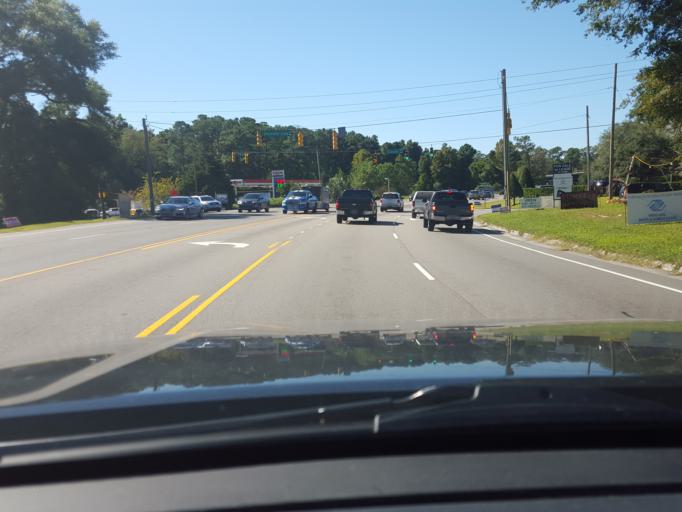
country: US
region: North Carolina
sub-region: New Hanover County
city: Seagate
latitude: 34.2108
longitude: -77.8364
